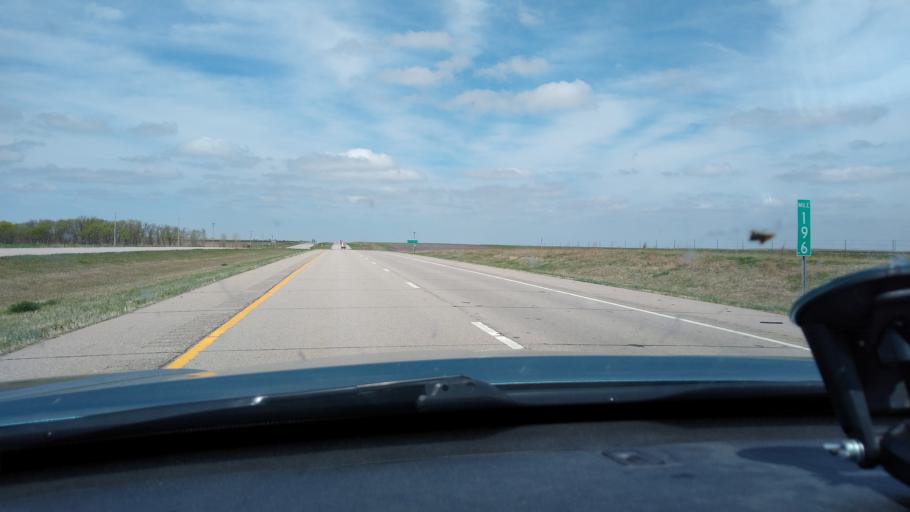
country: US
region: Kansas
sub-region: Cloud County
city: Concordia
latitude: 39.4631
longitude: -97.6666
